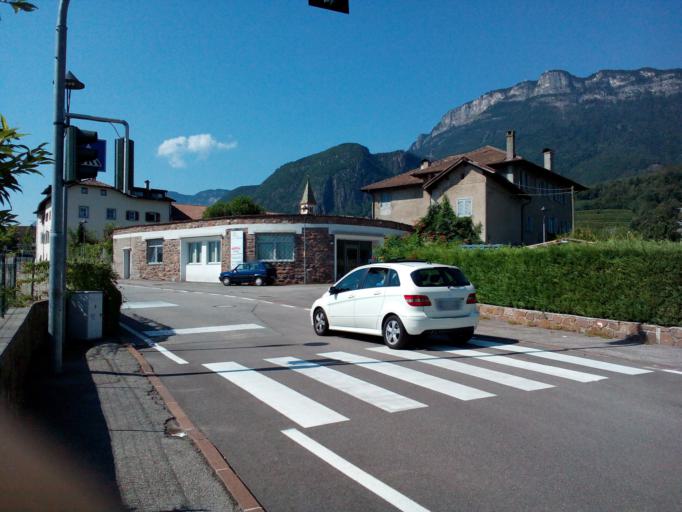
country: IT
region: Trentino-Alto Adige
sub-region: Bolzano
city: San Michele
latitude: 46.4566
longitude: 11.2630
